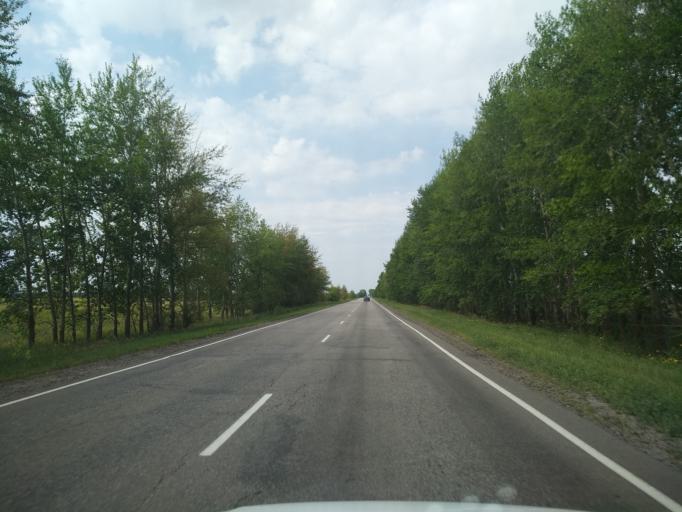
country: RU
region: Voronezj
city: Pereleshino
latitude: 51.7179
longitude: 40.0206
